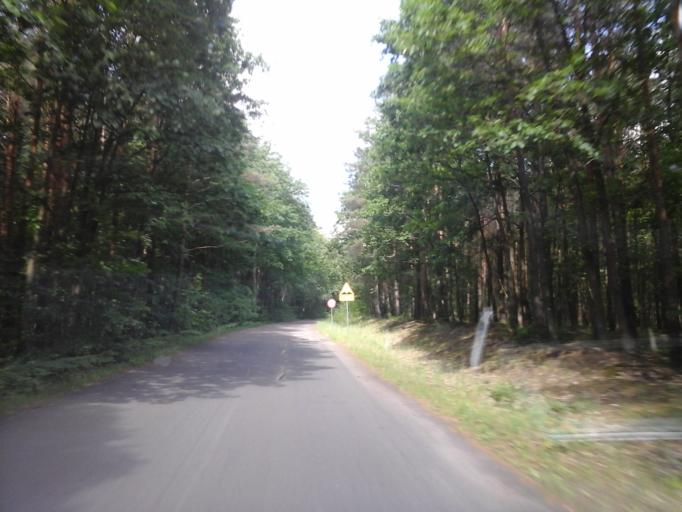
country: PL
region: Lubusz
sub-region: Powiat strzelecko-drezdenecki
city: Dobiegniew
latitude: 53.0824
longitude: 15.7757
